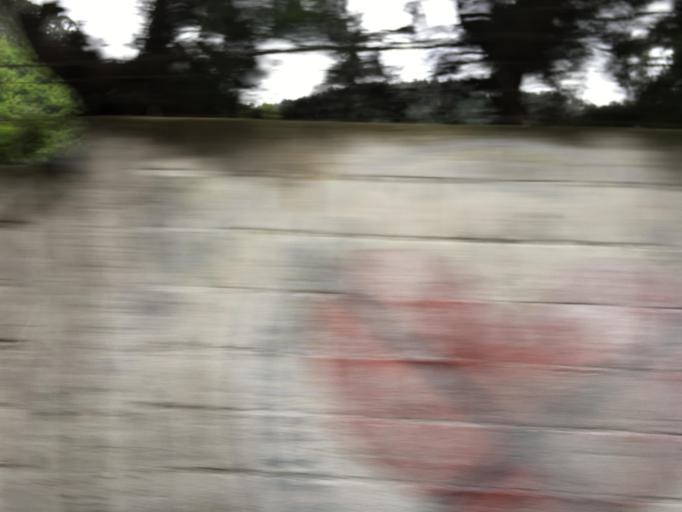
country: GT
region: Sacatepequez
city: Pastores
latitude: 14.6017
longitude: -90.7606
